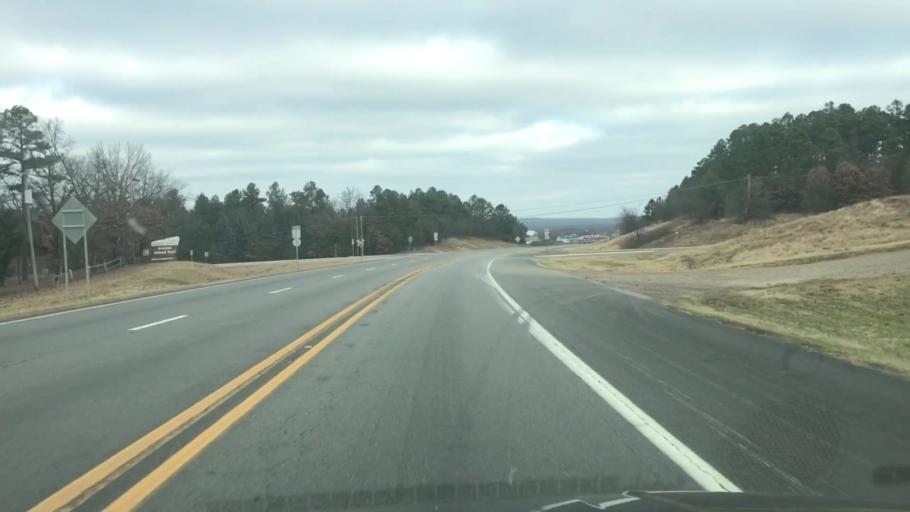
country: US
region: Arkansas
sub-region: Scott County
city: Waldron
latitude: 34.8868
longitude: -94.1075
